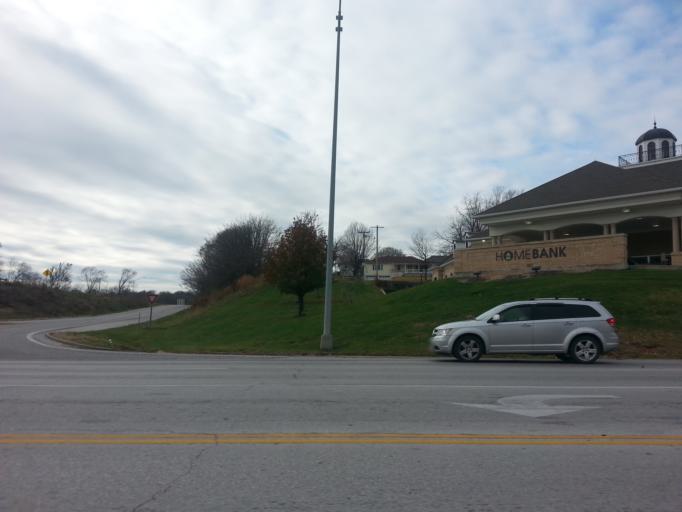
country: US
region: Missouri
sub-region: Marion County
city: Hannibal
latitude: 39.7153
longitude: -91.3920
